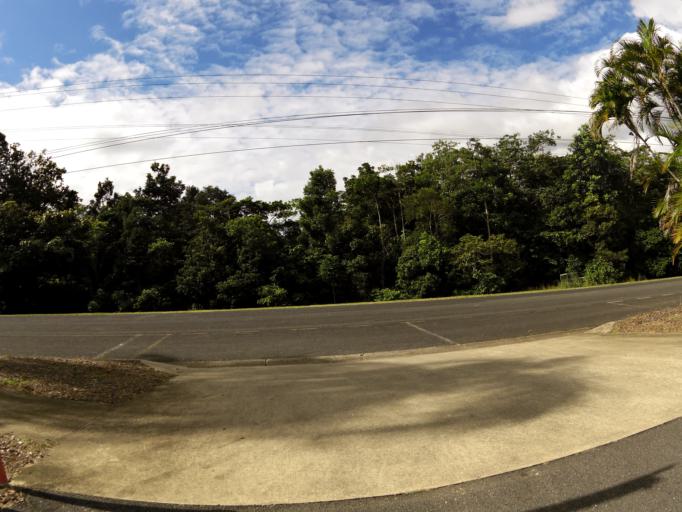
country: AU
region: Queensland
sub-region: Tablelands
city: Kuranda
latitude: -16.8217
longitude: 145.6399
